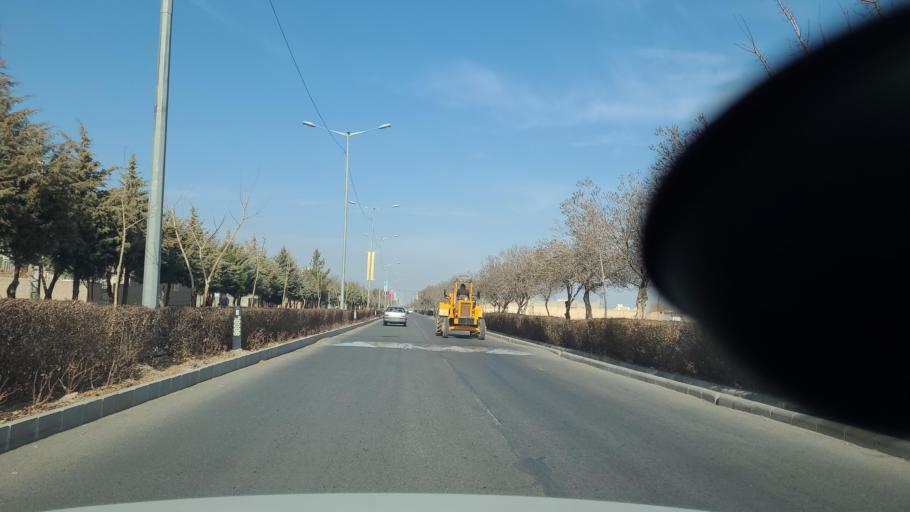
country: IR
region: Razavi Khorasan
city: Fariman
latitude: 35.6854
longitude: 59.8435
